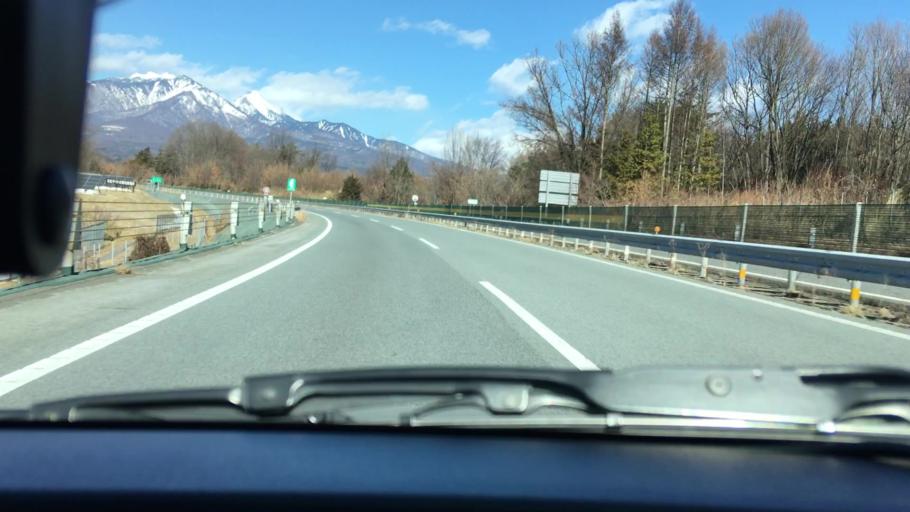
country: JP
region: Yamanashi
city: Nirasaki
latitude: 35.8216
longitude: 138.3946
